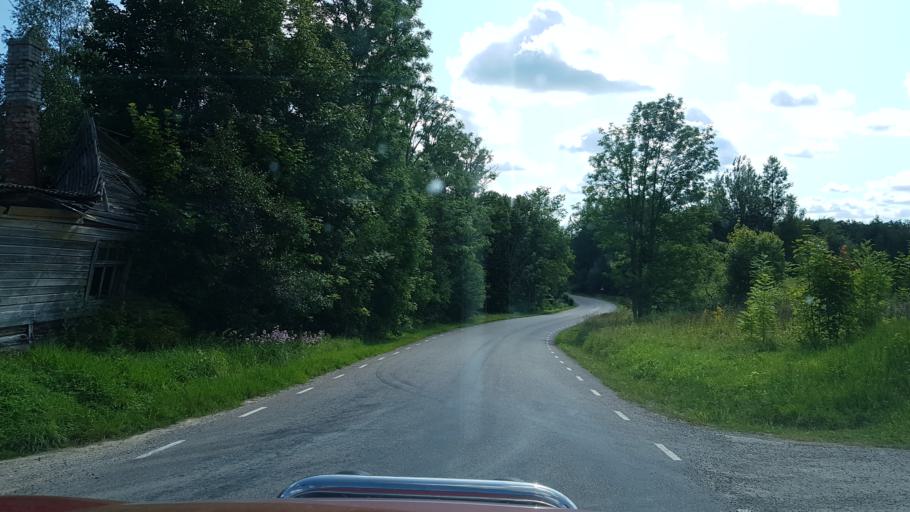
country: EE
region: Vorumaa
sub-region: Voru linn
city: Voru
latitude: 57.6724
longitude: 27.0822
